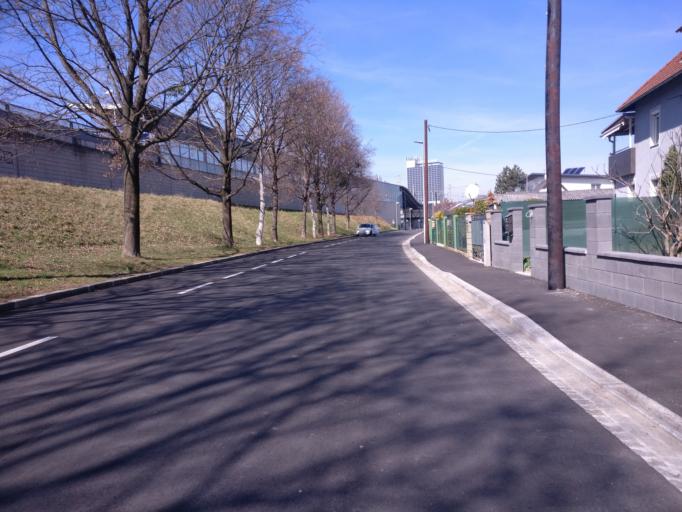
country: AT
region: Styria
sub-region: Graz Stadt
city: Wetzelsdorf
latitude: 47.0576
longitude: 15.4207
